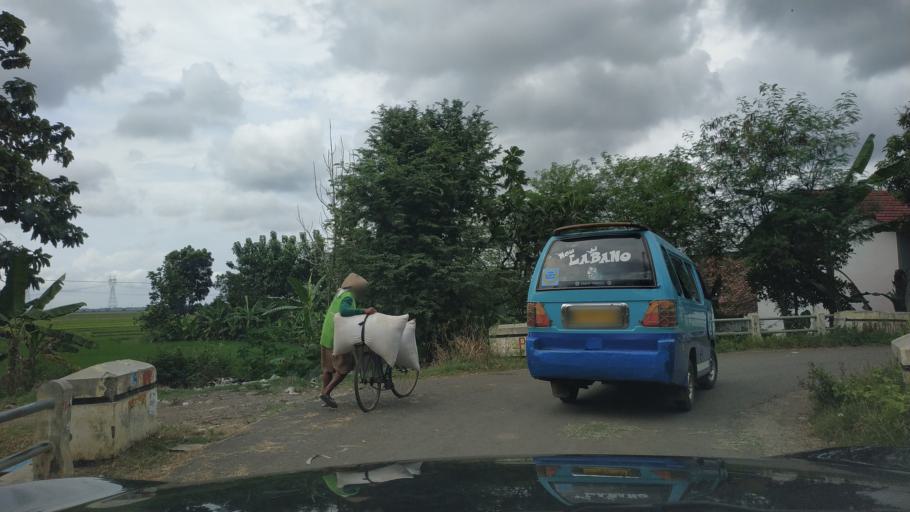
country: ID
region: Central Java
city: Pemalang
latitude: -6.9469
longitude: 109.3494
